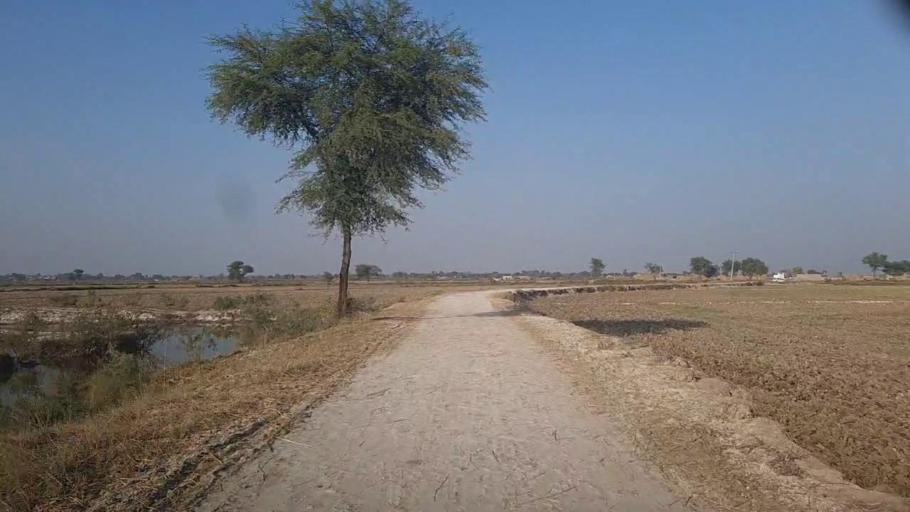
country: PK
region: Sindh
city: Thul
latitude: 28.1620
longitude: 68.8139
